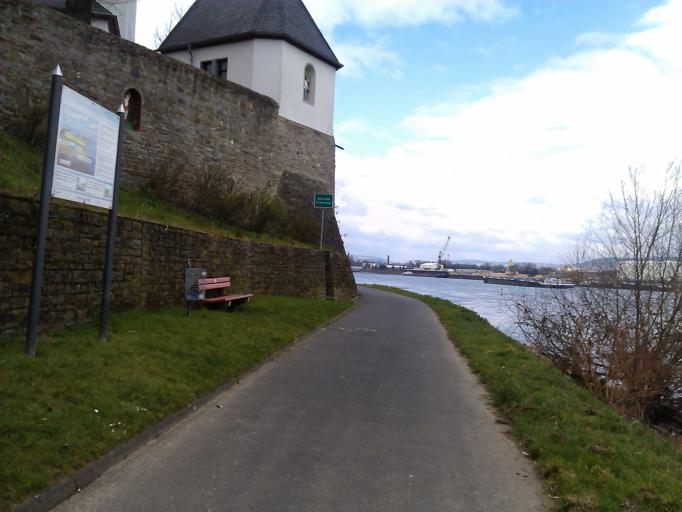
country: DE
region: Rheinland-Pfalz
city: Sankt Sebastian
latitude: 50.4110
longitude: 7.5671
